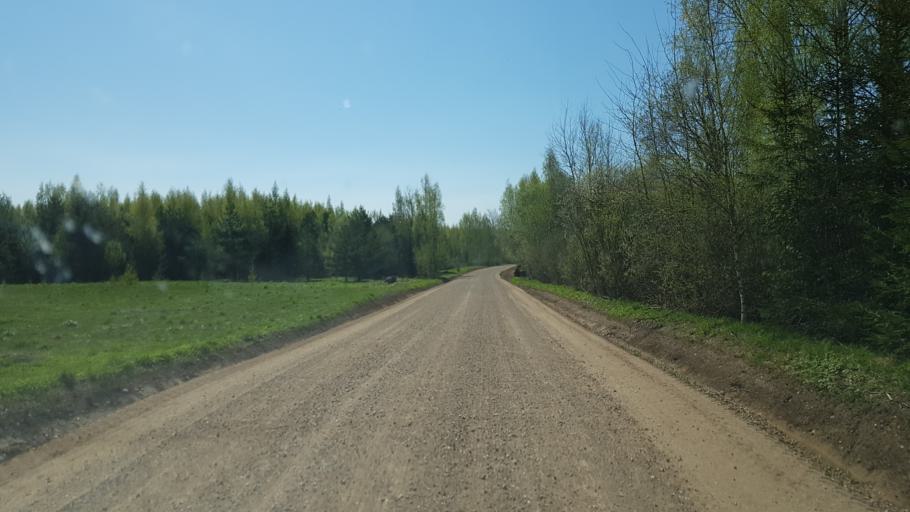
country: EE
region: Polvamaa
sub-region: Polva linn
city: Polva
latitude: 58.1155
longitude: 27.2386
